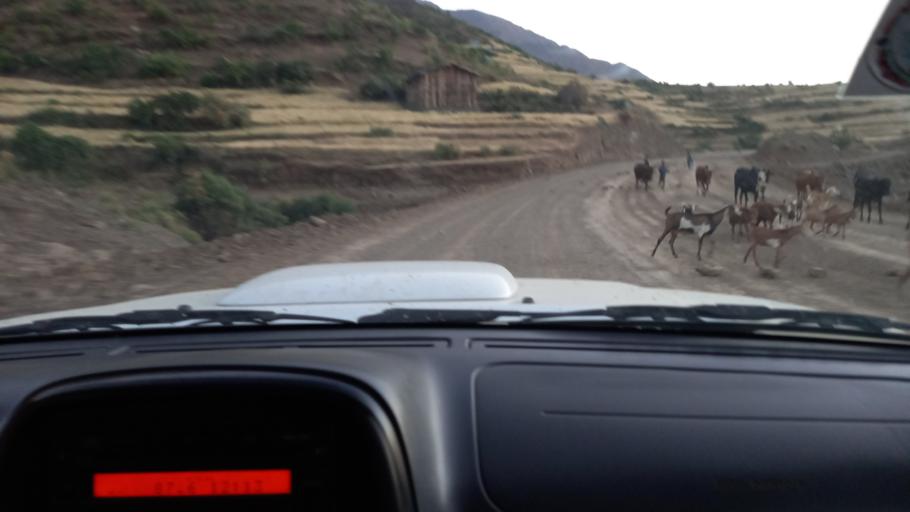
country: ET
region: Amhara
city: Debark'
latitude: 13.0358
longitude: 38.0556
